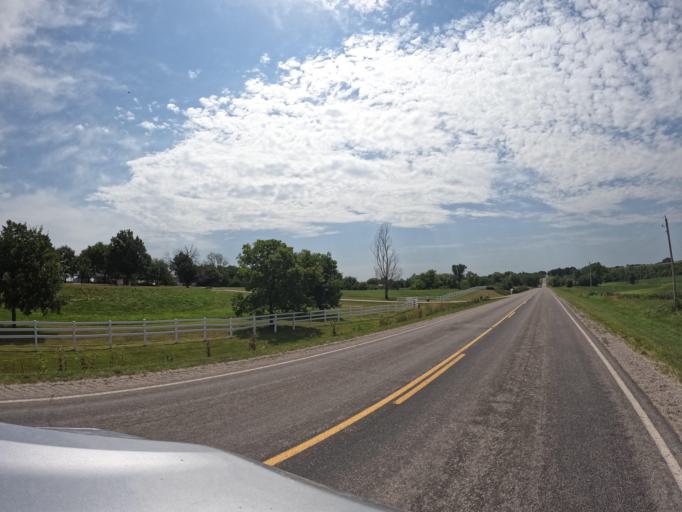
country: US
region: Iowa
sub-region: Appanoose County
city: Centerville
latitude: 40.8015
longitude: -92.9448
